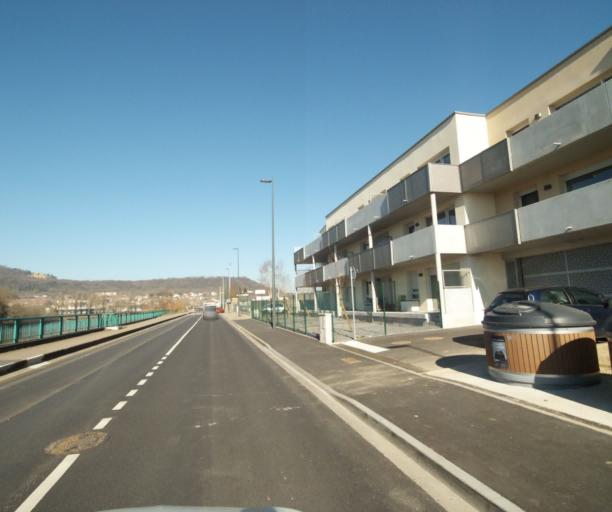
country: FR
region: Lorraine
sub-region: Departement de Meurthe-et-Moselle
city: Malzeville
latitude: 48.7112
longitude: 6.1789
